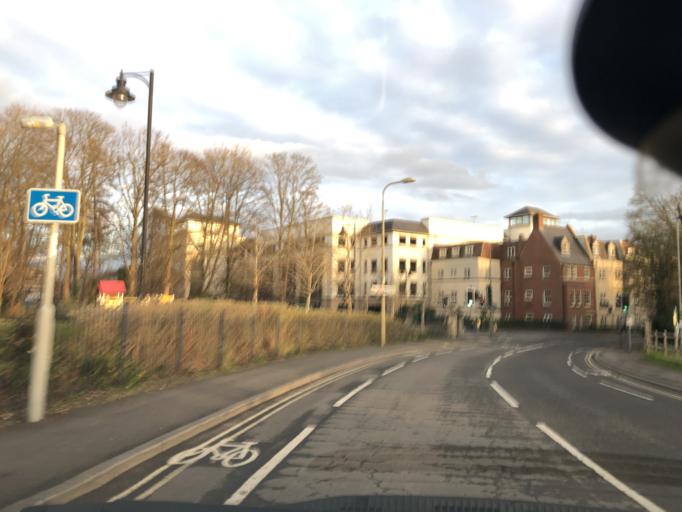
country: GB
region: England
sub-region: Oxfordshire
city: Witney
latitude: 51.7883
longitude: -1.4884
